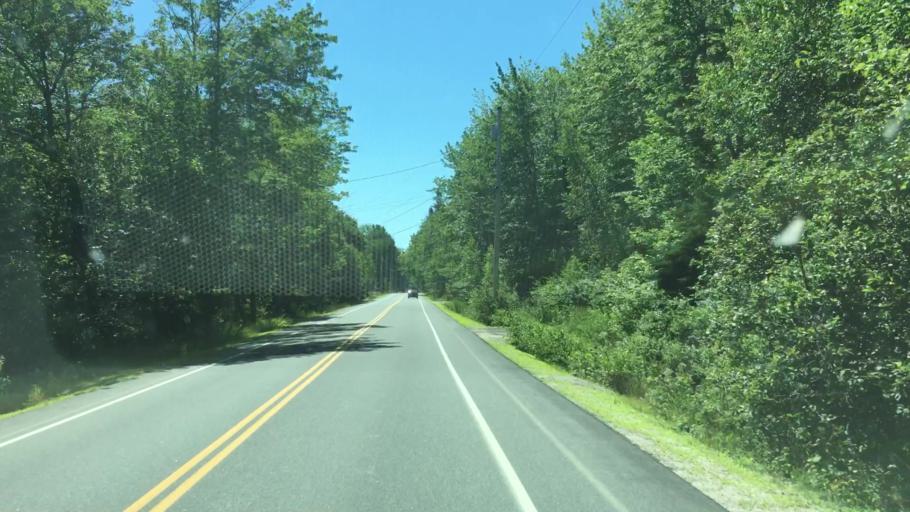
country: US
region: Maine
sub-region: Hancock County
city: Sedgwick
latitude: 44.4133
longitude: -68.6060
